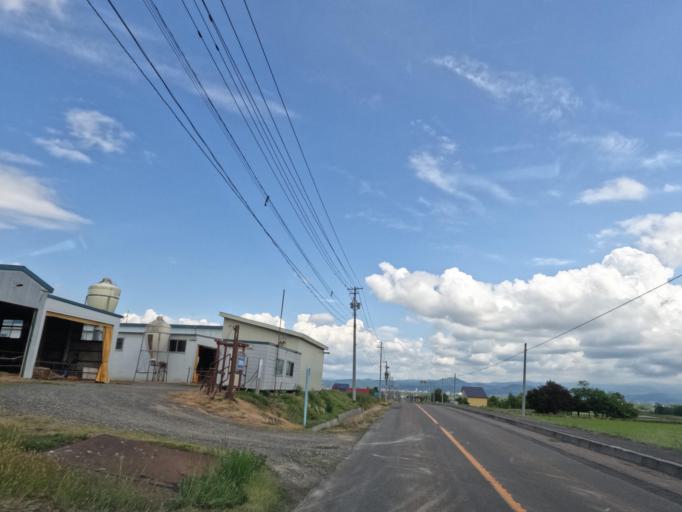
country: JP
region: Hokkaido
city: Takikawa
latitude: 43.5779
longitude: 141.8416
